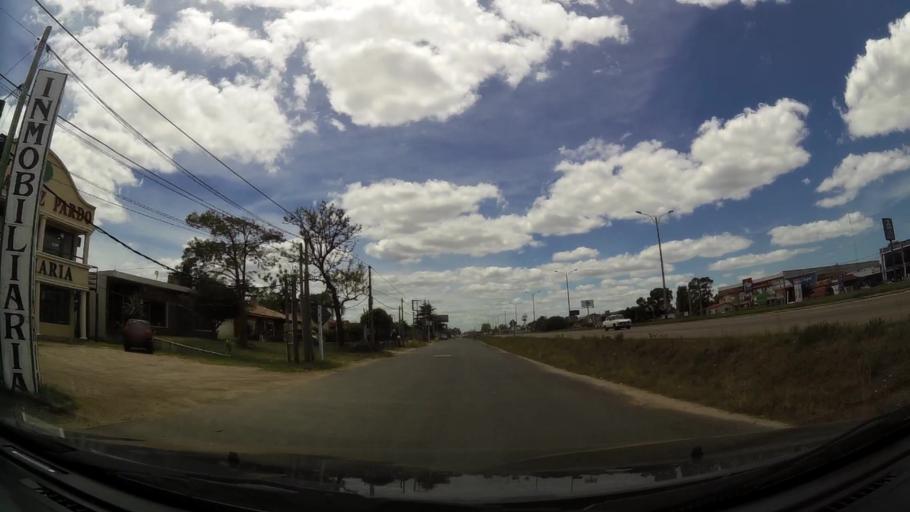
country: UY
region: Canelones
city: Barra de Carrasco
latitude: -34.8307
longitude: -55.9748
